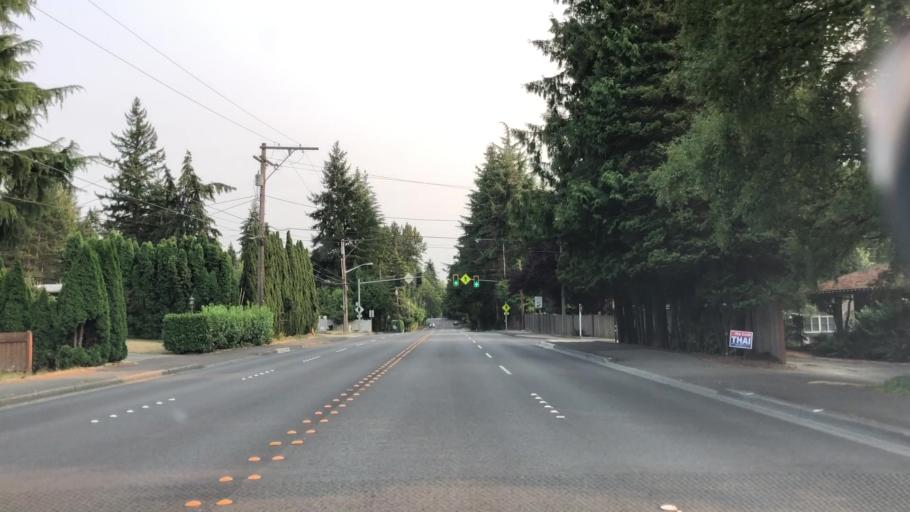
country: US
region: Washington
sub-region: King County
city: Mercer Island
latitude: 47.5716
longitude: -122.2270
